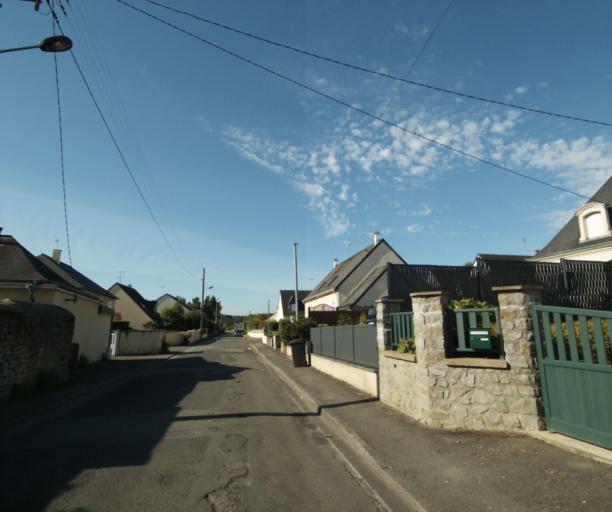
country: FR
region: Pays de la Loire
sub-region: Departement de la Mayenne
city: Laval
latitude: 48.0565
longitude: -0.7626
